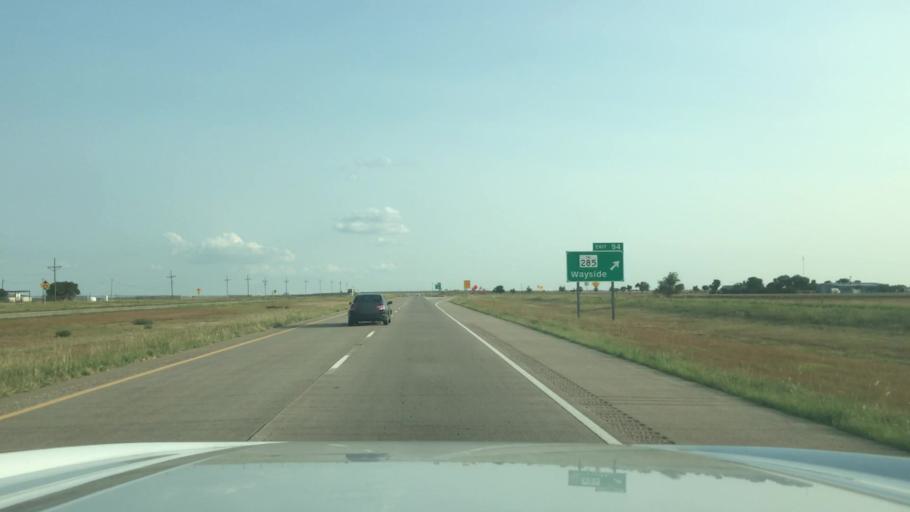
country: US
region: Texas
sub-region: Randall County
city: Canyon
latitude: 34.8164
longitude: -101.8489
